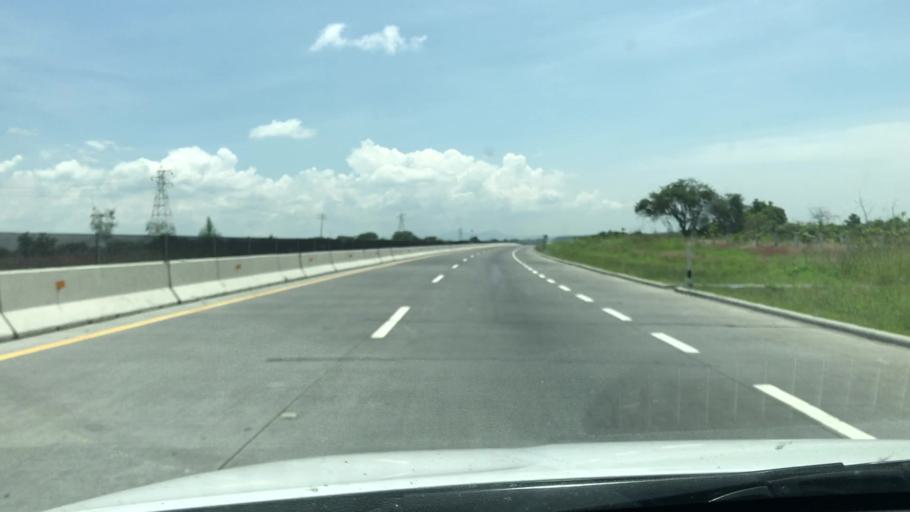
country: MX
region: Michoacan
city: La Piedad Cavadas
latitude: 20.3903
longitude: -102.1037
